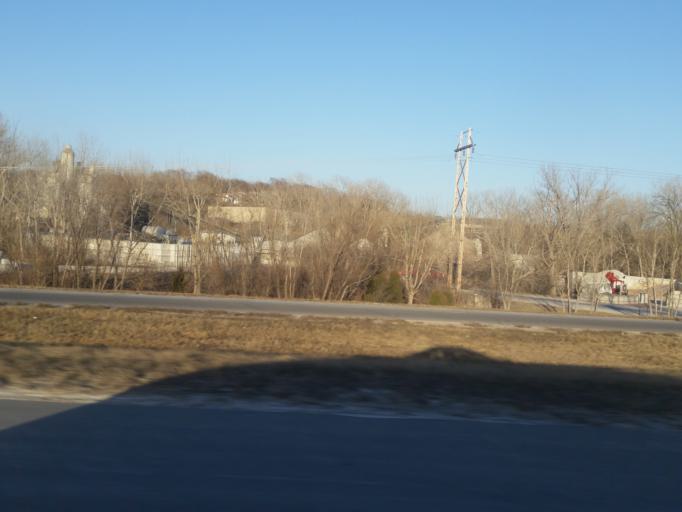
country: US
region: Nebraska
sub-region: Sarpy County
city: Offutt Air Force Base
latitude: 41.1420
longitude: -95.9378
